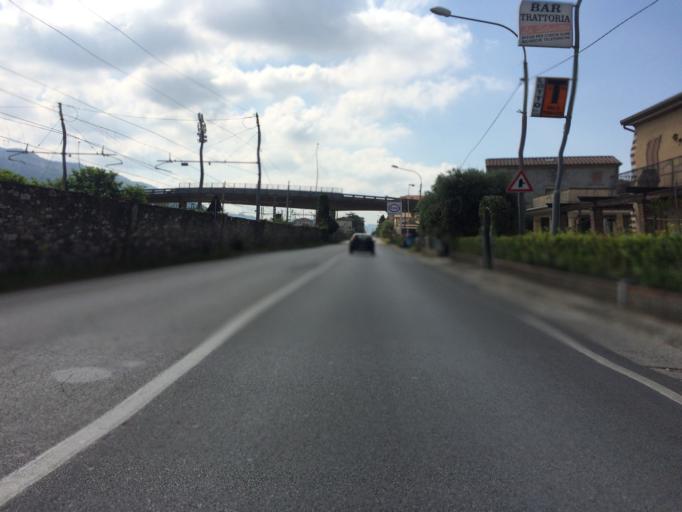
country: IT
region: Tuscany
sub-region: Provincia di Lucca
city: Ripa-Pozzi-Querceta-Ponterosso
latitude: 43.9800
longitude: 10.1961
